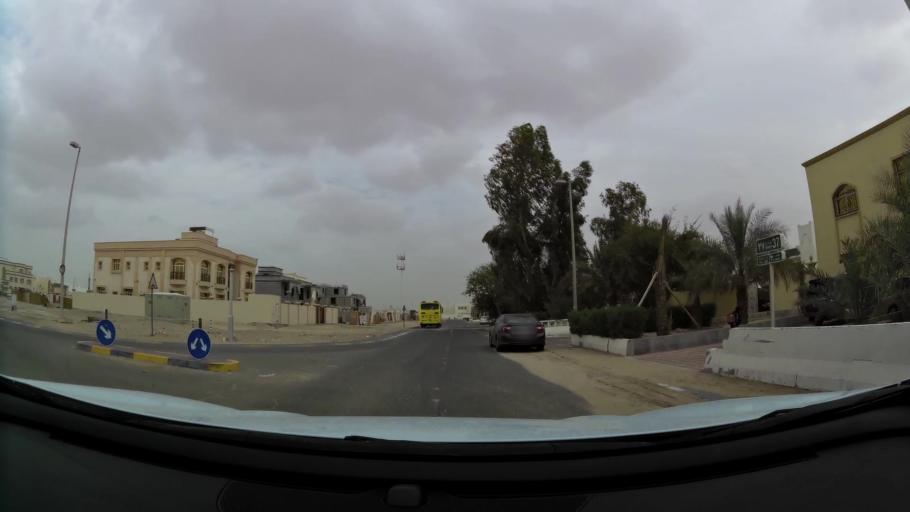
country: AE
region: Abu Dhabi
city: Abu Dhabi
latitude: 24.3472
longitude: 54.6473
